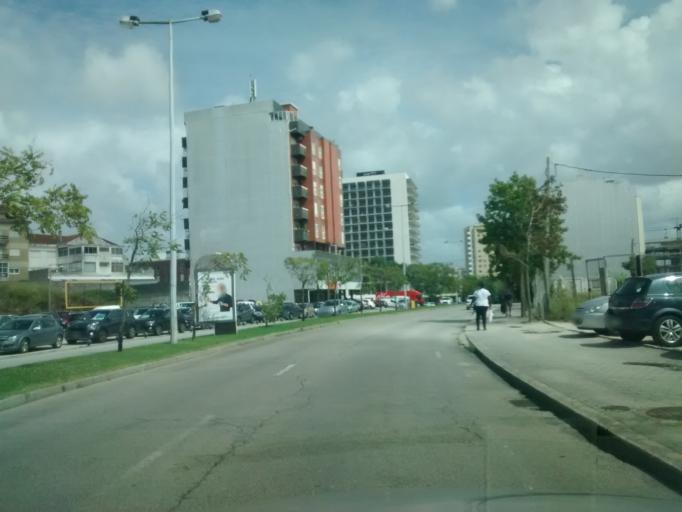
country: PT
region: Aveiro
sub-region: Aveiro
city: Aveiro
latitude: 40.6419
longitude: -8.6449
